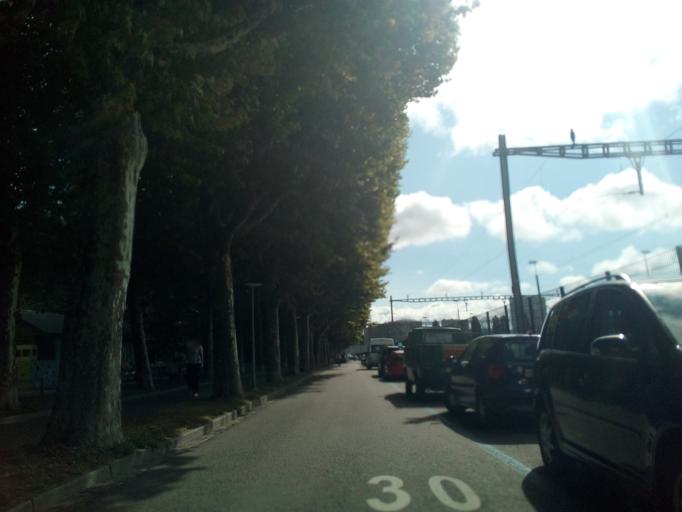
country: FR
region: Alsace
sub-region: Departement du Haut-Rhin
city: Village-Neuf
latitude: 47.5794
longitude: 7.5890
